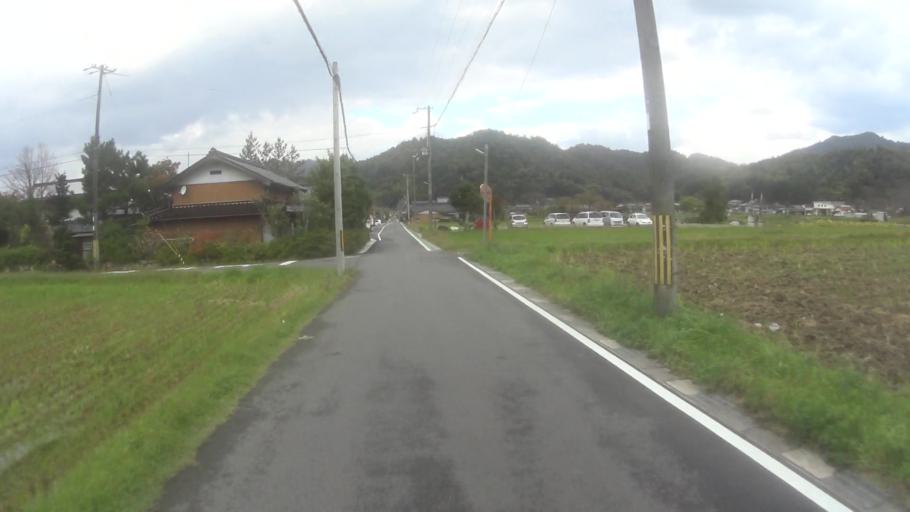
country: JP
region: Kyoto
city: Miyazu
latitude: 35.5246
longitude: 135.1264
